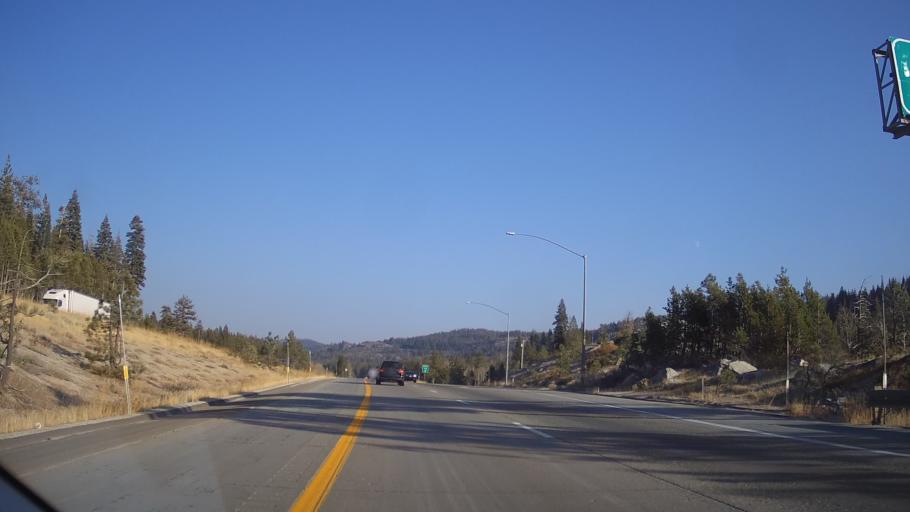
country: US
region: California
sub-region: Nevada County
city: Truckee
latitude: 39.3118
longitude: -120.5042
